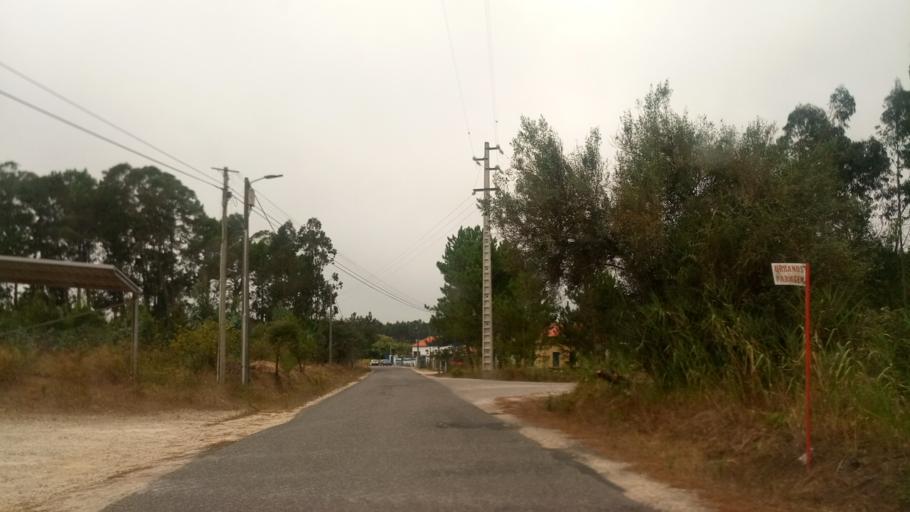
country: PT
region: Leiria
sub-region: Caldas da Rainha
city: Caldas da Rainha
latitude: 39.4252
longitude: -9.1521
